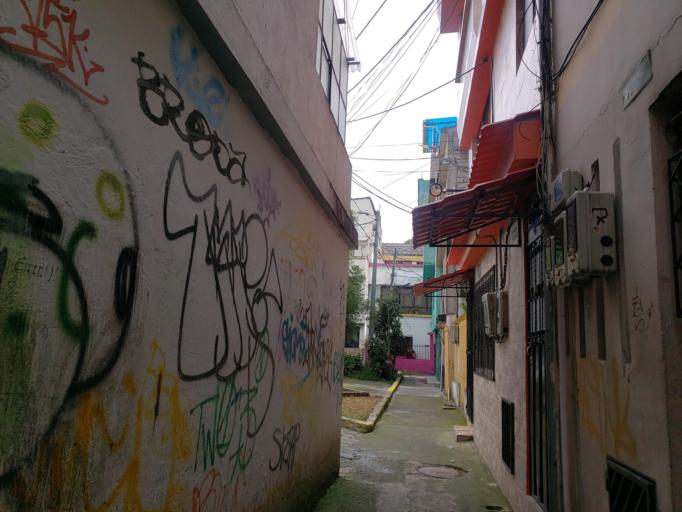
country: EC
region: Pichincha
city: Quito
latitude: -0.2683
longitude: -78.5412
